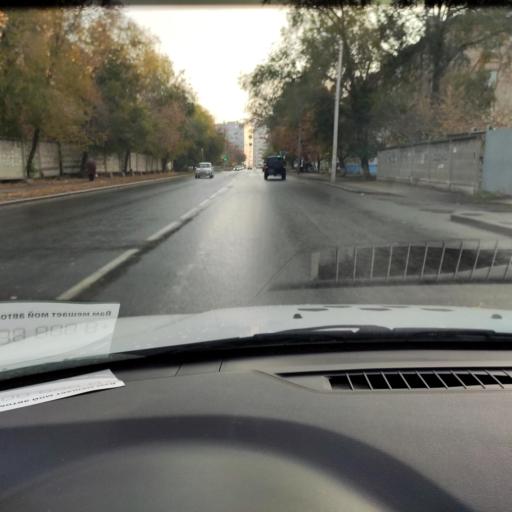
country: RU
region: Samara
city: Tol'yatti
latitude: 53.5189
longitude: 49.4136
